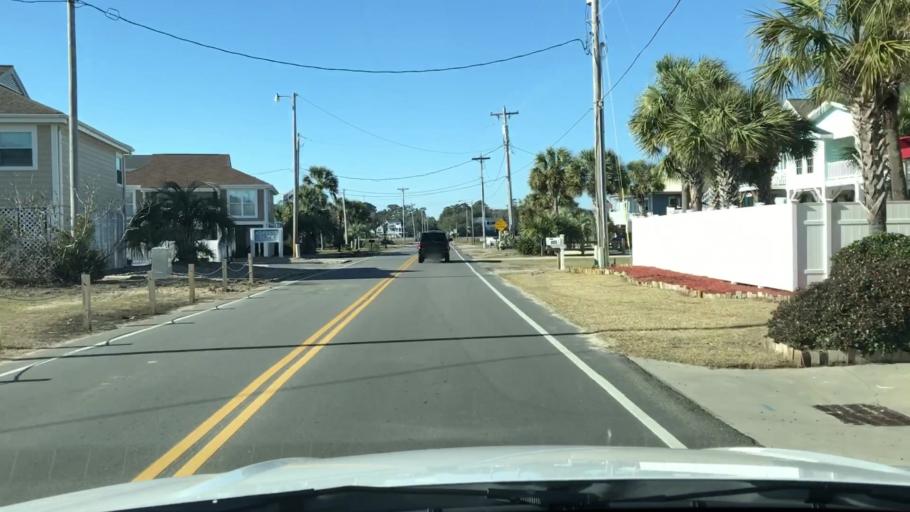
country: US
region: South Carolina
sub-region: Horry County
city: Garden City
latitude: 33.5811
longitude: -78.9953
